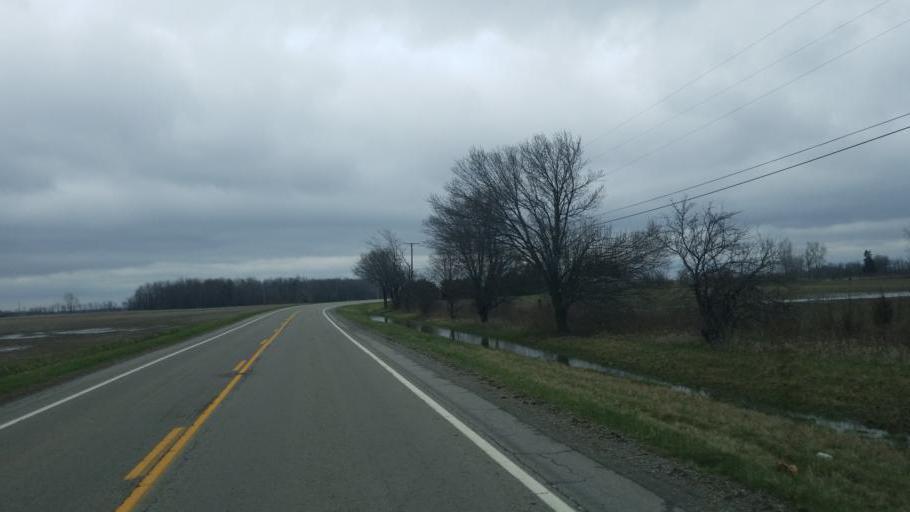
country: US
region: Ohio
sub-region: Hardin County
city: Forest
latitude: 40.7276
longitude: -83.5569
